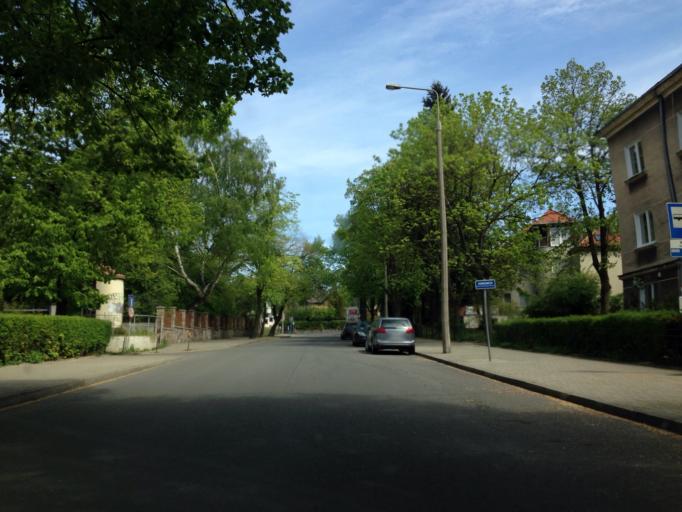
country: PL
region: Pomeranian Voivodeship
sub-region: Gdynia
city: Gdynia
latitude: 54.5103
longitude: 18.5461
